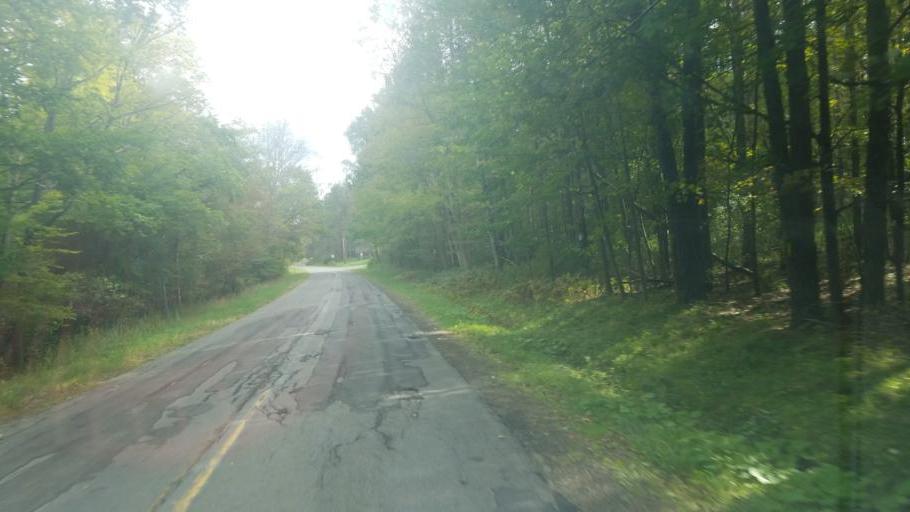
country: US
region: New York
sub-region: Cattaraugus County
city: Weston Mills
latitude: 42.1031
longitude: -78.3391
